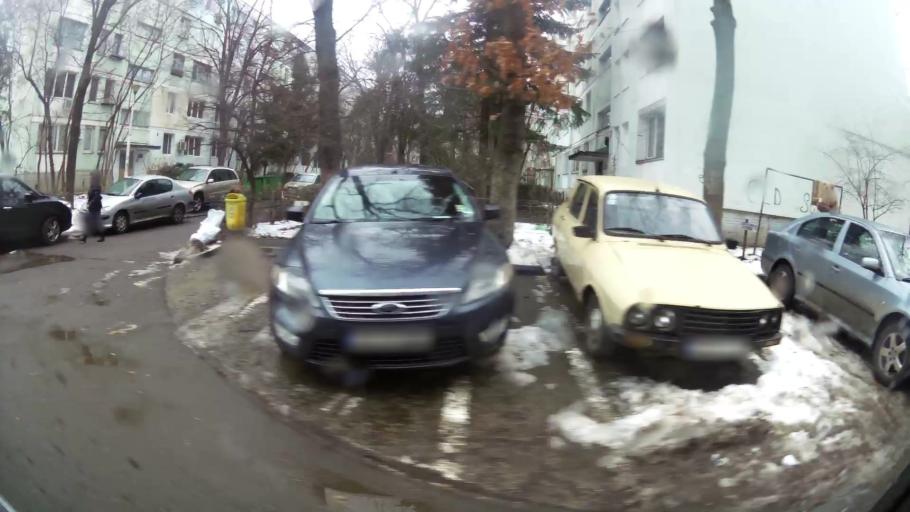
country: RO
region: Ilfov
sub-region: Comuna Chiajna
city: Rosu
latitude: 44.4235
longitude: 26.0198
